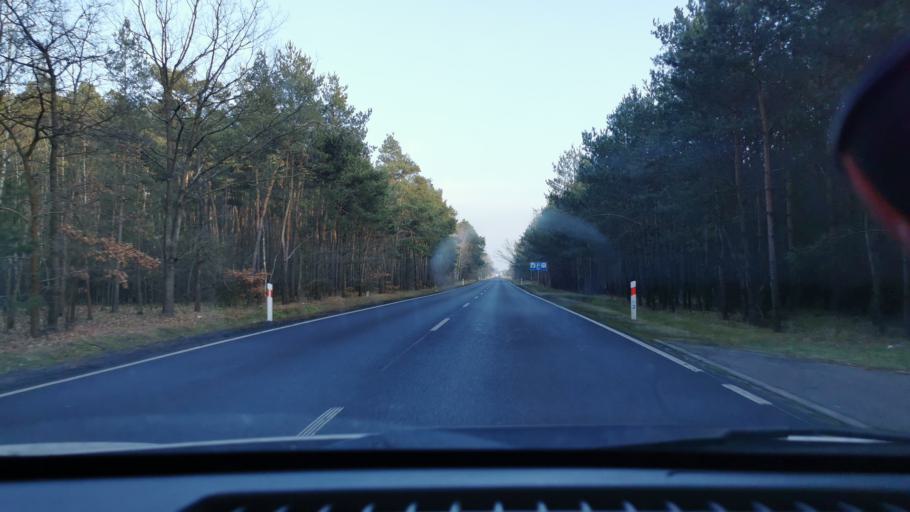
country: PL
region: Lodz Voivodeship
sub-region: Powiat pabianicki
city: Dlutow
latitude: 51.5114
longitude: 19.3546
